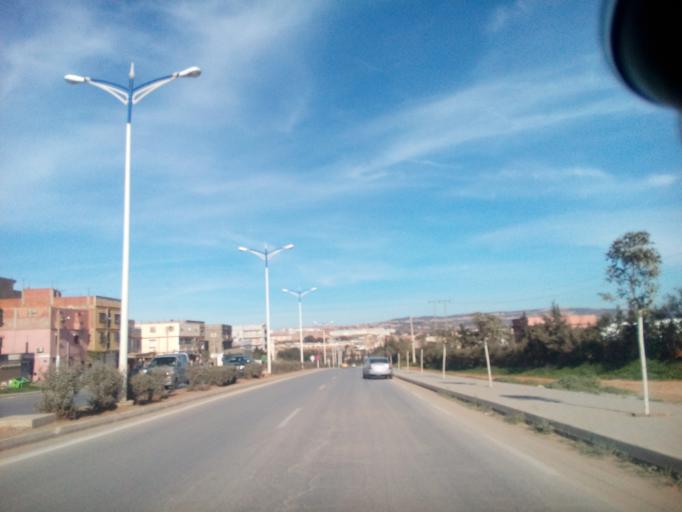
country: DZ
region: Mostaganem
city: Mostaganem
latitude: 35.9334
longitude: 0.1196
